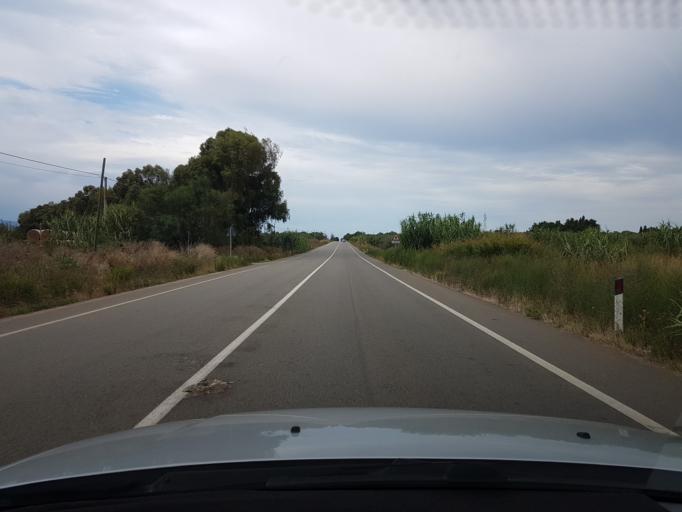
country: IT
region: Sardinia
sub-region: Provincia di Oristano
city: Nuraxinieddu
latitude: 39.9544
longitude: 8.6115
